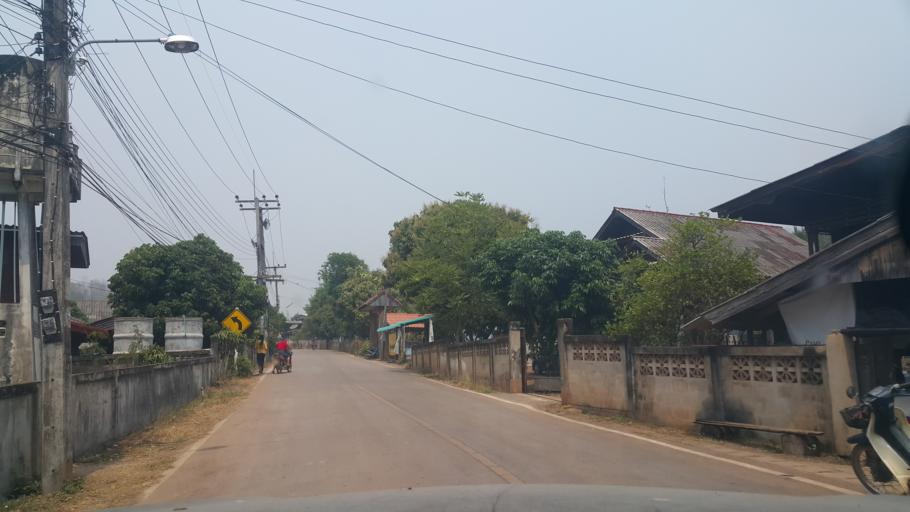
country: TH
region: Lampang
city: Soem Ngam
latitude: 18.1916
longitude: 99.1955
